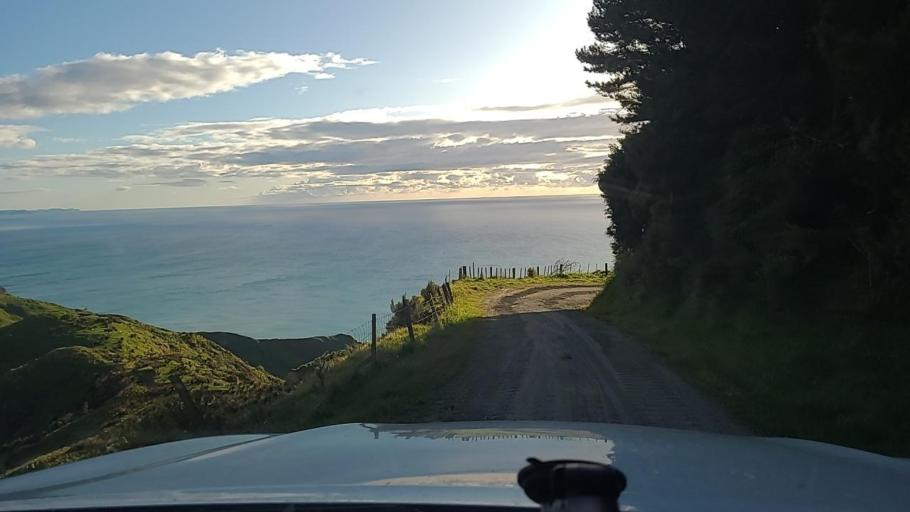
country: NZ
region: Gisborne
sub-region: Gisborne District
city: Gisborne
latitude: -38.9468
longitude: 177.8910
